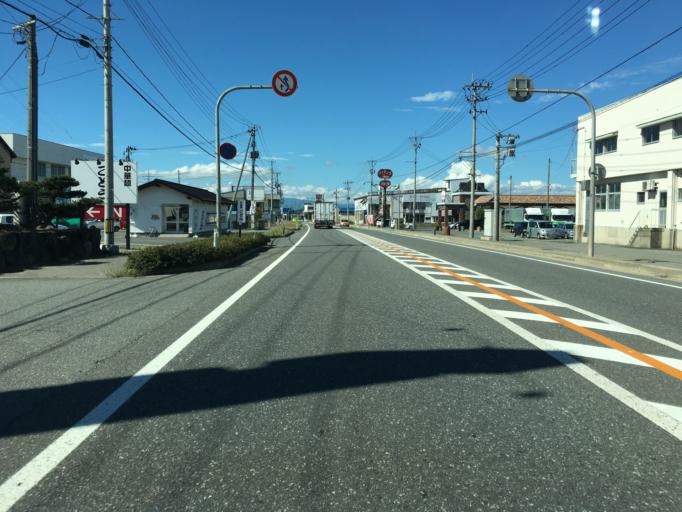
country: JP
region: Yamagata
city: Yonezawa
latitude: 37.9150
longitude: 140.1332
